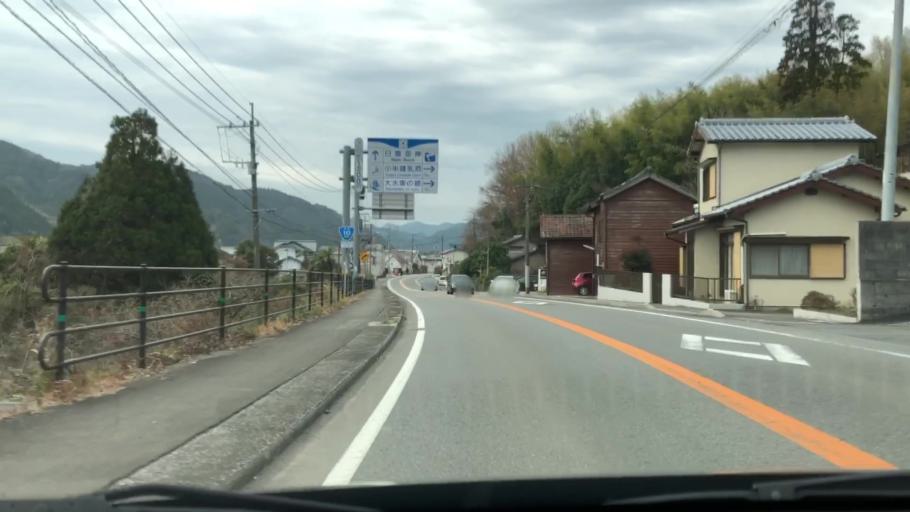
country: JP
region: Oita
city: Saiki
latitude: 32.9798
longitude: 131.8471
